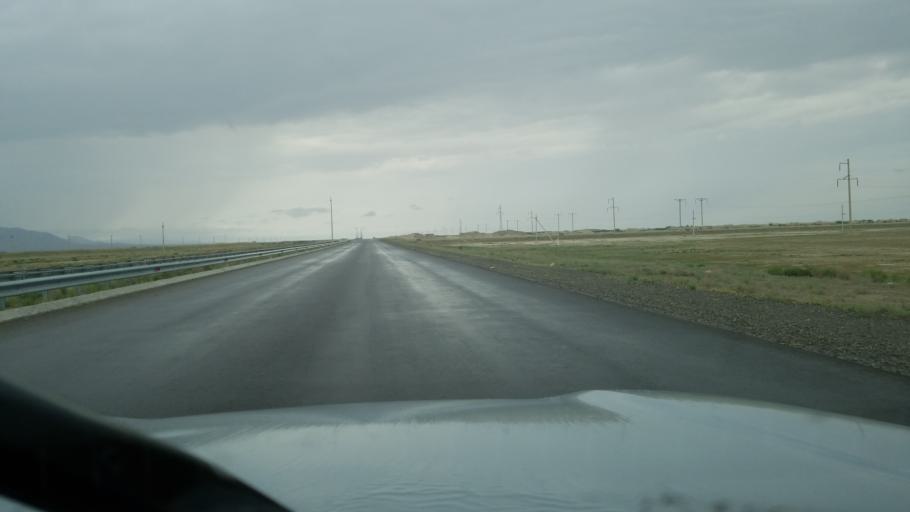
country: TM
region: Balkan
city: Serdar
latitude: 39.0354
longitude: 56.1690
